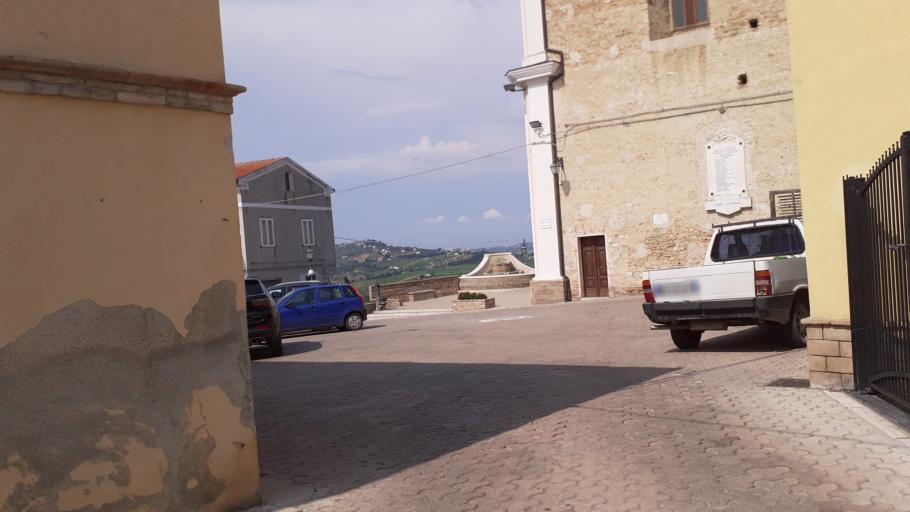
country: IT
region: Abruzzo
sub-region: Provincia di Chieti
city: Vacri
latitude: 42.2970
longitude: 14.2318
